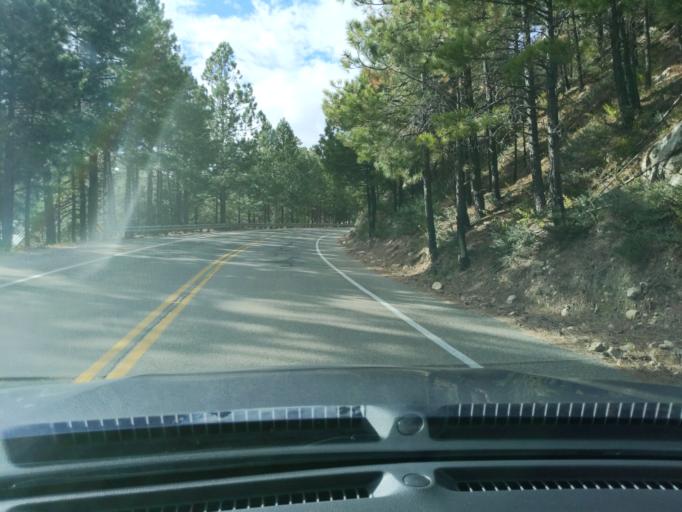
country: US
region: Arizona
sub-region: Pinal County
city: Oracle
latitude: 32.4468
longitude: -110.7630
